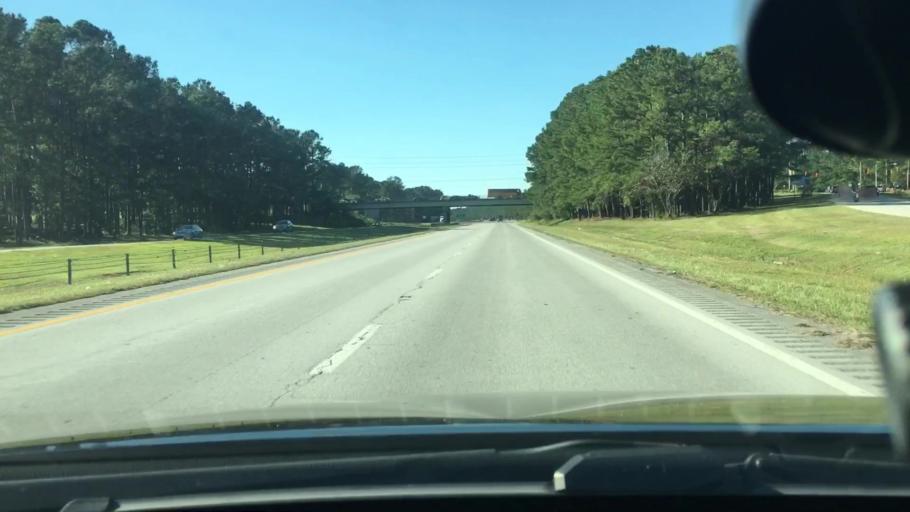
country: US
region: North Carolina
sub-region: Craven County
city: Trent Woods
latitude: 35.1112
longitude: -77.0950
